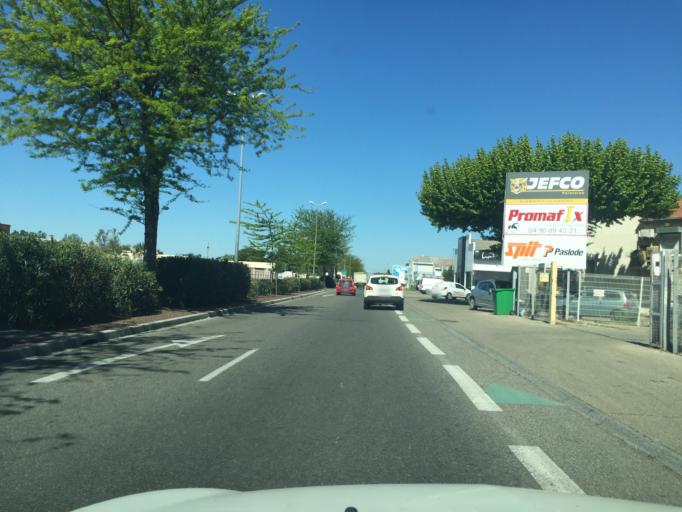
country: FR
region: Provence-Alpes-Cote d'Azur
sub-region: Departement du Vaucluse
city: Montfavet
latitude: 43.9362
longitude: 4.8467
